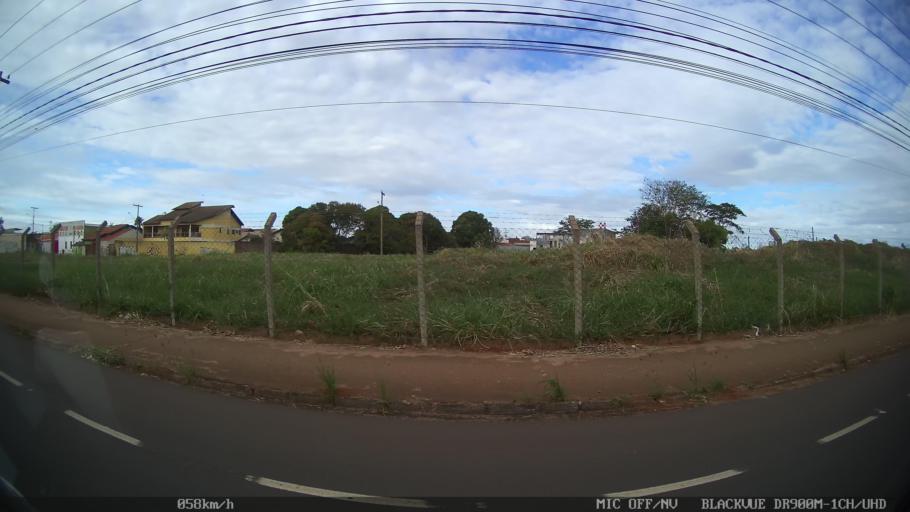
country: BR
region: Sao Paulo
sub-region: Sao Jose Do Rio Preto
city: Sao Jose do Rio Preto
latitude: -20.8243
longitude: -49.4143
